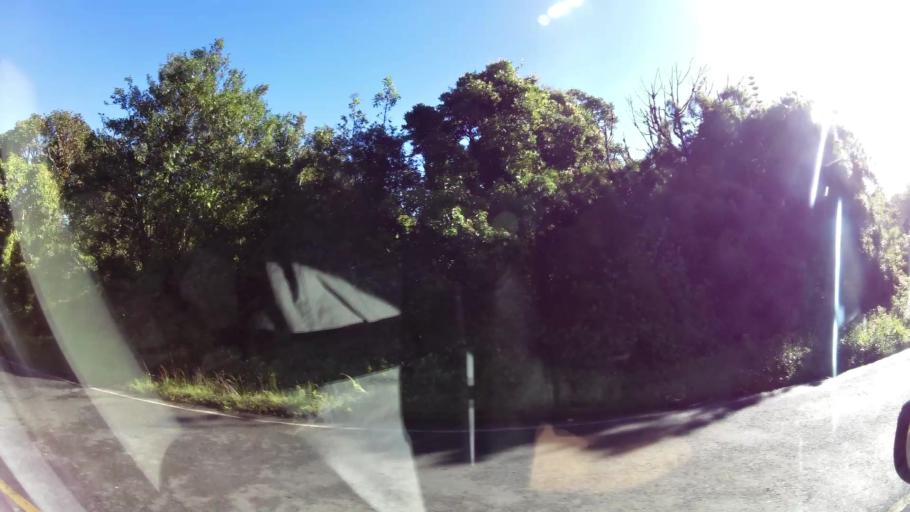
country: CR
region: San Jose
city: San Marcos
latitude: 9.7046
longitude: -83.9465
